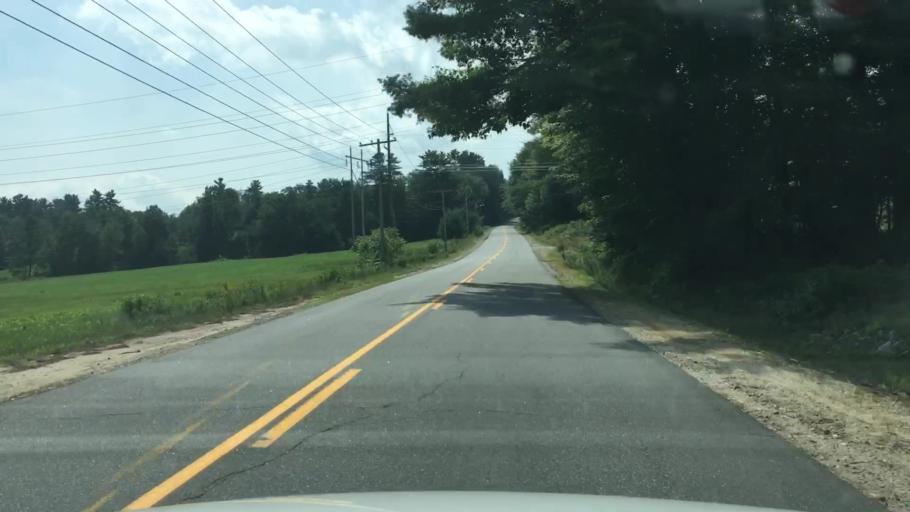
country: US
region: Maine
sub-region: Oxford County
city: Rumford
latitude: 44.5232
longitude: -70.5122
